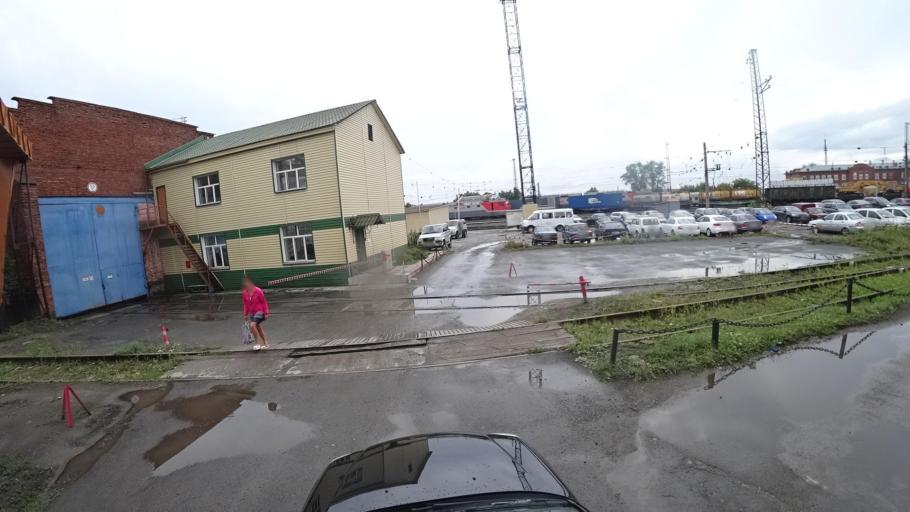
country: RU
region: Sverdlovsk
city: Kamyshlov
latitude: 56.8502
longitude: 62.7091
